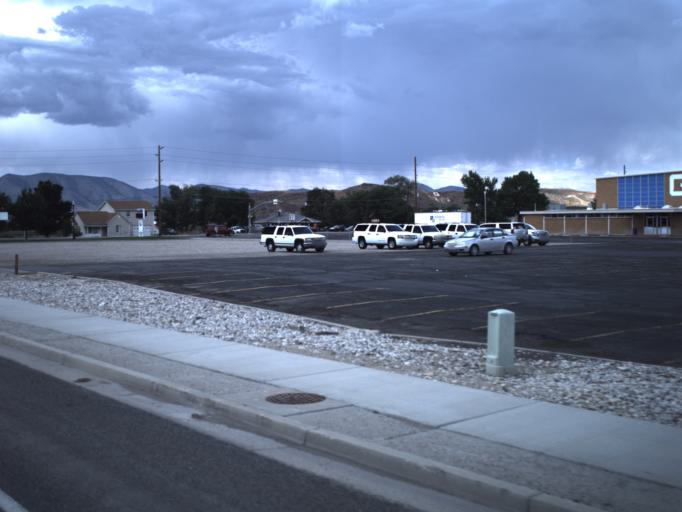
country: US
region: Utah
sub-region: Sanpete County
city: Gunnison
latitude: 39.1419
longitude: -111.8172
